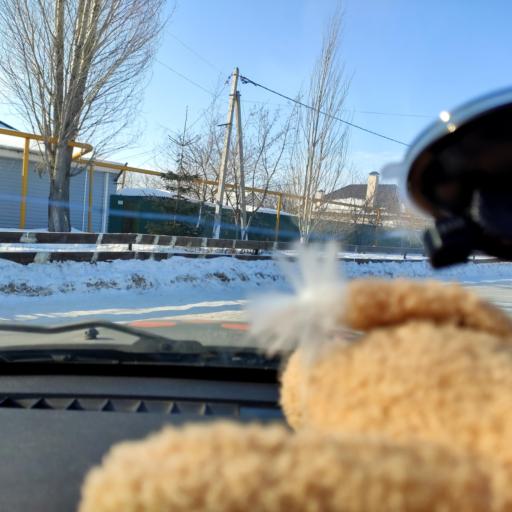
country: RU
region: Samara
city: Podstepki
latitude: 53.5135
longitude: 49.1241
